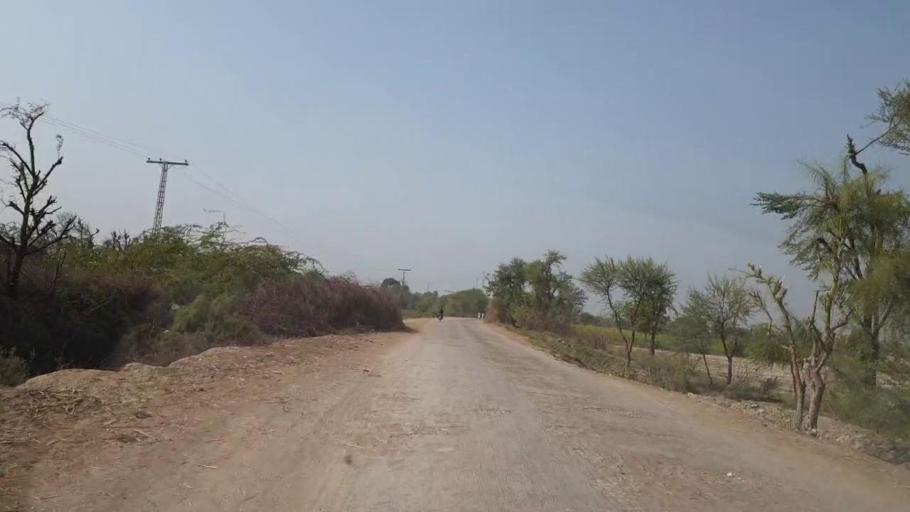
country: PK
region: Sindh
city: Mirpur Khas
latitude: 25.7030
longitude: 69.1371
